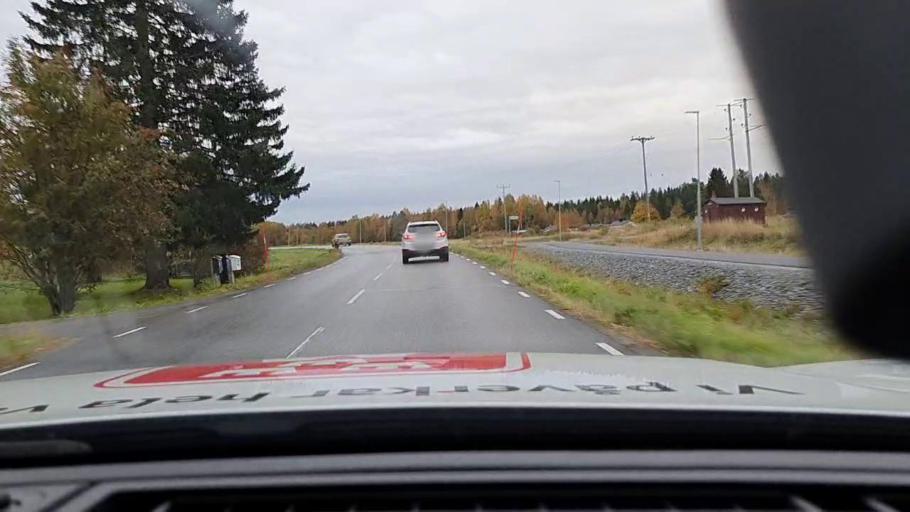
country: SE
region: Norrbotten
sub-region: Bodens Kommun
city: Saevast
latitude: 65.7681
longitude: 21.7105
